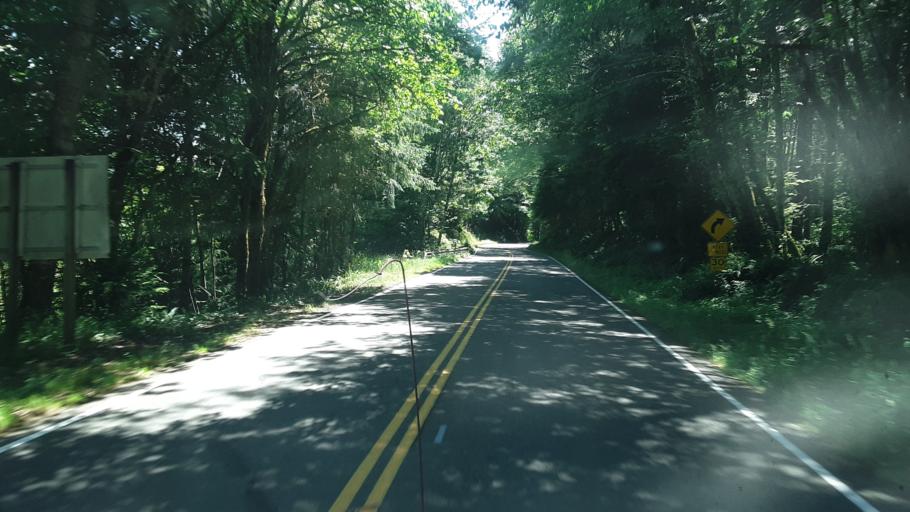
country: US
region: Washington
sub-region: Clark County
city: Yacolt
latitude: 46.0720
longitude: -122.2025
